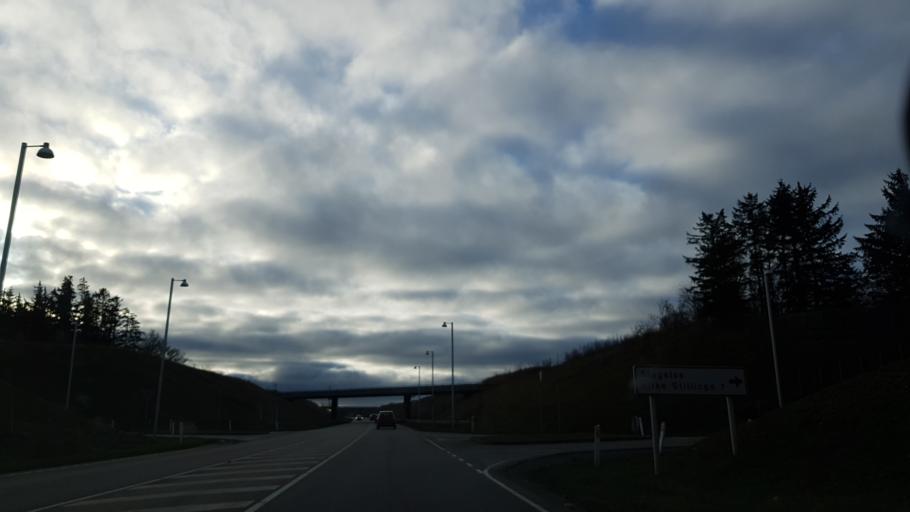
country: DK
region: Zealand
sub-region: Slagelse Kommune
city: Slagelse
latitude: 55.4146
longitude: 11.3249
